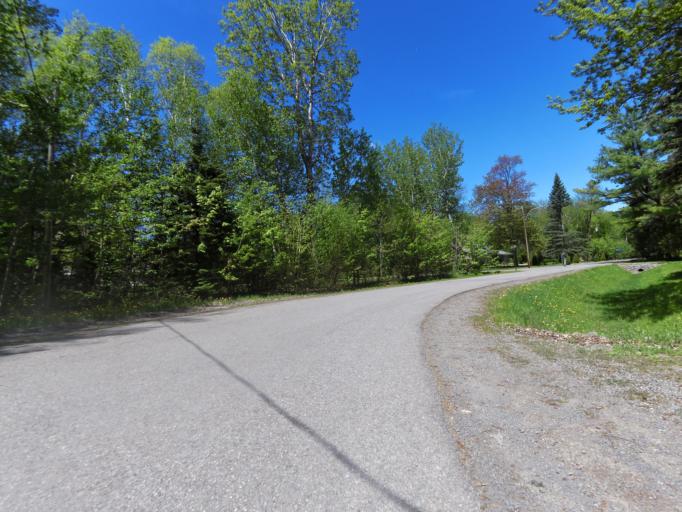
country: CA
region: Ontario
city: Ottawa
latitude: 45.4153
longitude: -75.7866
